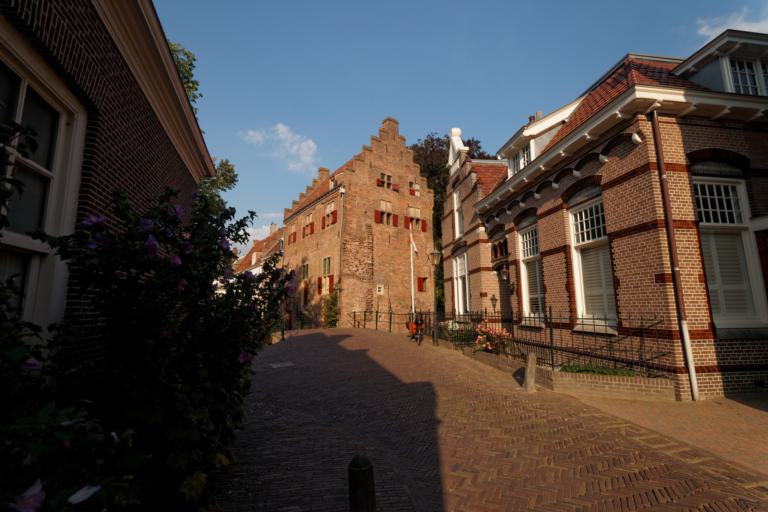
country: NL
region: Utrecht
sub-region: Gemeente Amersfoort
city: Amersfoort
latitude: 52.1543
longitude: 5.3911
